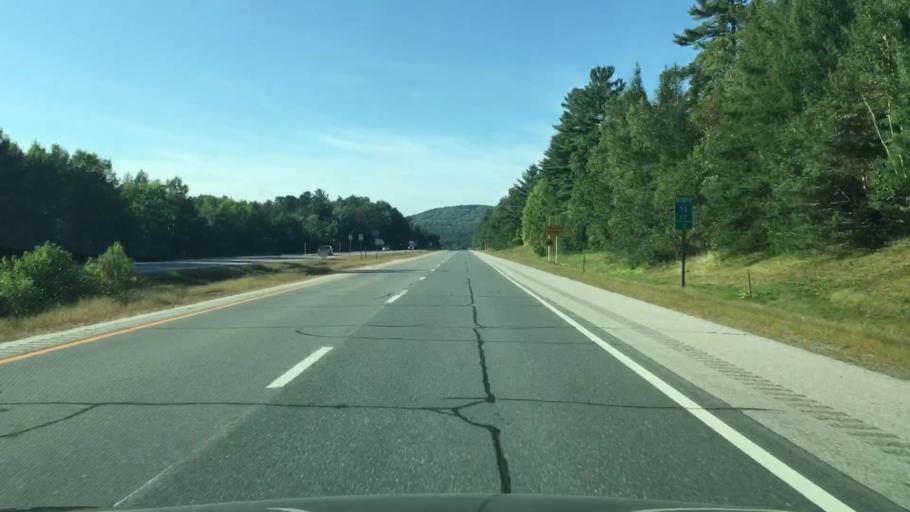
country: US
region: New Hampshire
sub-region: Grafton County
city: Littleton
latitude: 44.2335
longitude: -71.7533
